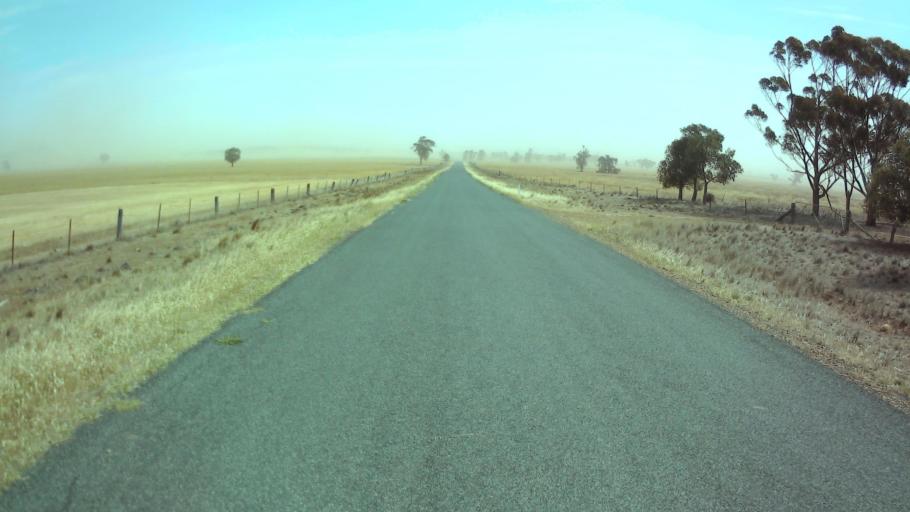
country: AU
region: New South Wales
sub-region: Weddin
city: Grenfell
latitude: -33.7441
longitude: 147.9928
